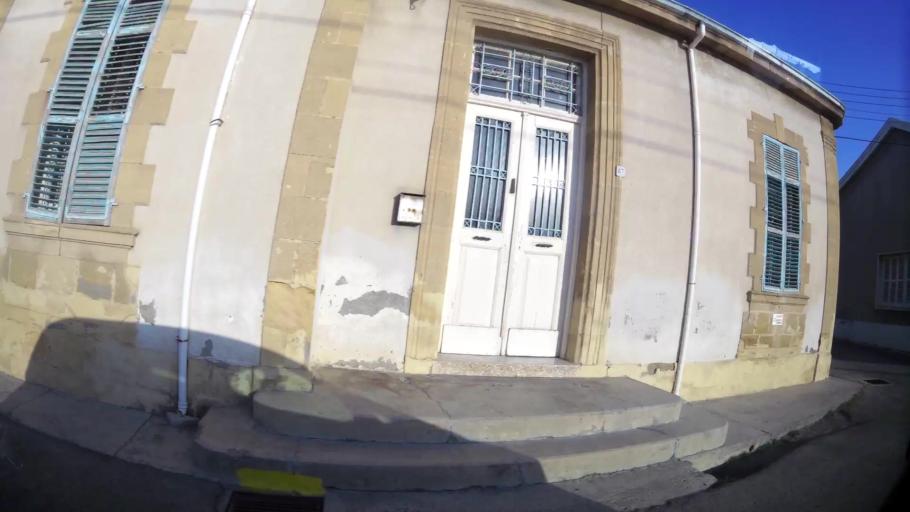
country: CY
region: Lefkosia
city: Nicosia
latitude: 35.1641
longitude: 33.3364
